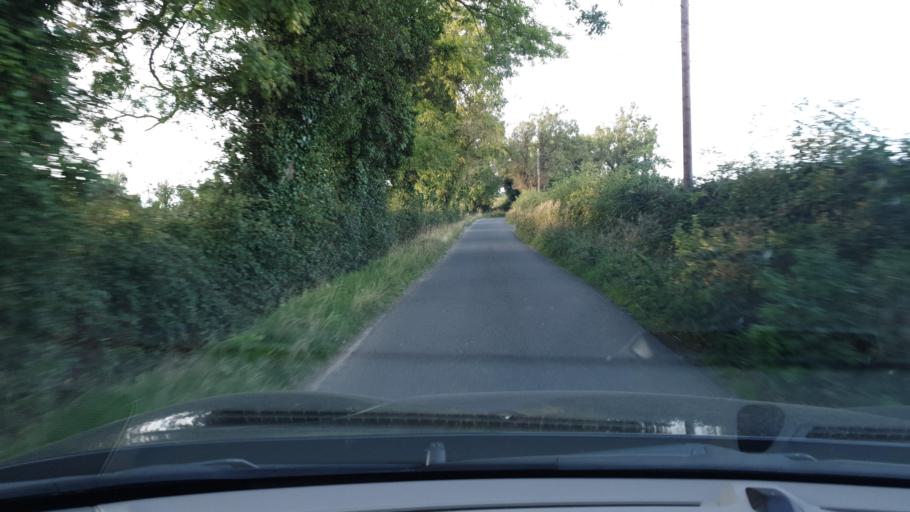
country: IE
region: Leinster
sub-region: An Mhi
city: Ashbourne
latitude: 53.5179
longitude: -6.3854
